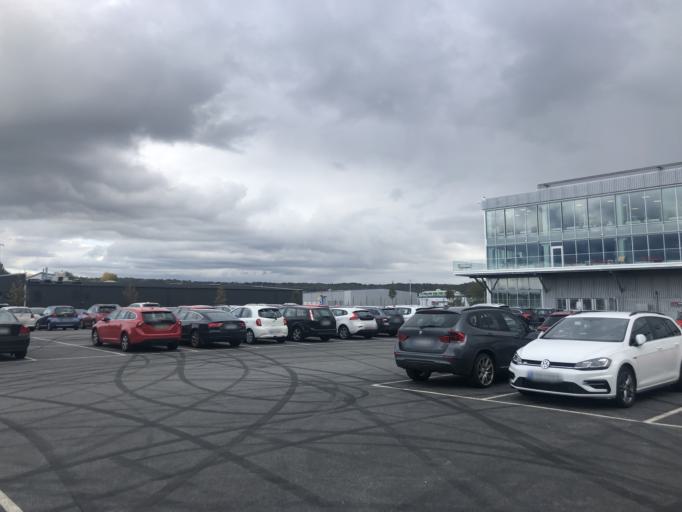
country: SE
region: Vaestra Goetaland
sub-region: Molndal
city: Moelndal
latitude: 57.6395
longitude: 12.0059
